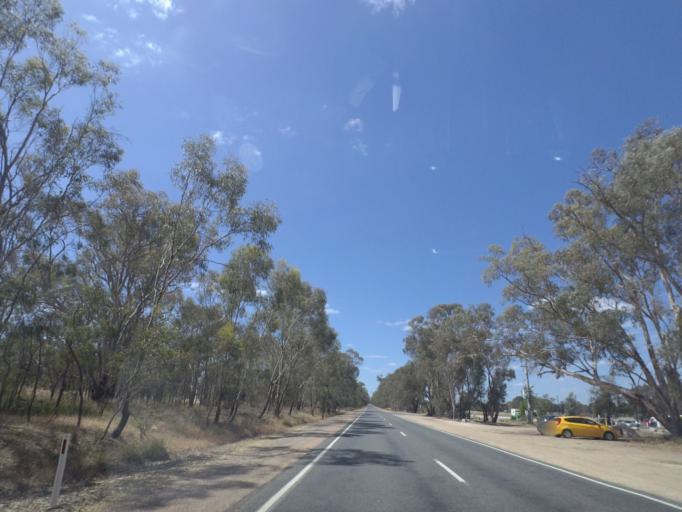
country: AU
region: Victoria
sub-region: Wangaratta
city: Wangaratta
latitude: -36.4389
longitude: 146.2473
